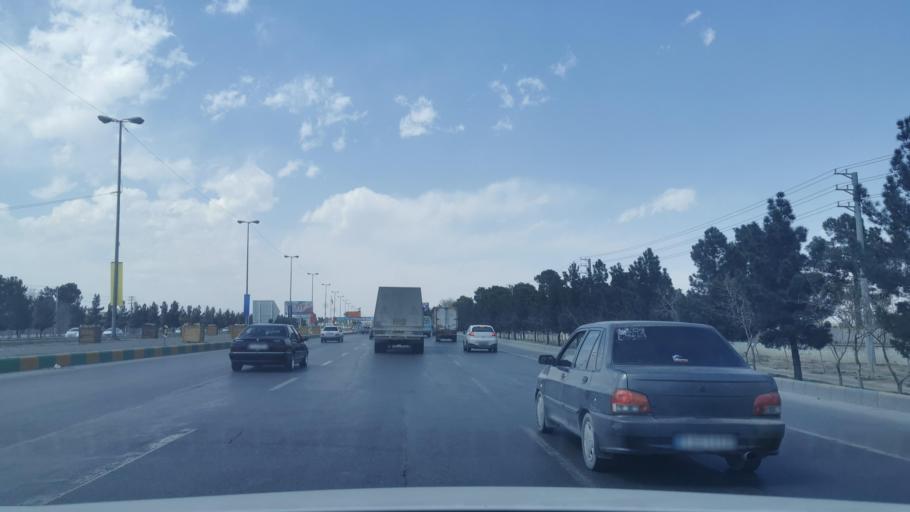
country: IR
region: Razavi Khorasan
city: Torqabeh
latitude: 36.4182
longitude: 59.4655
